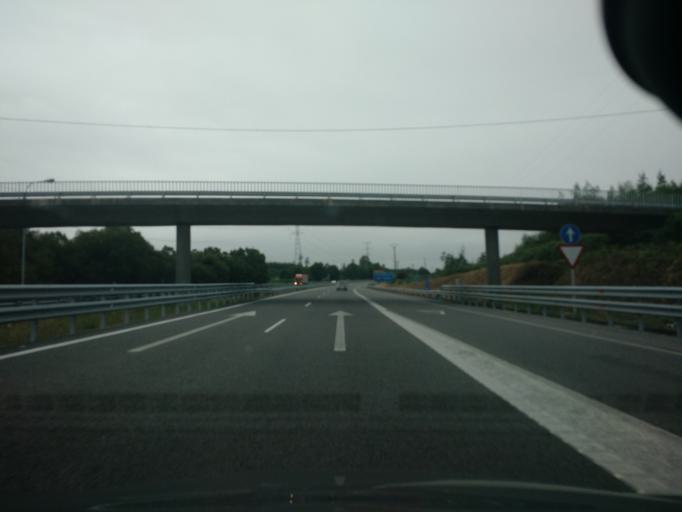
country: ES
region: Galicia
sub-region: Provincia da Coruna
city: Ordes
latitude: 43.0946
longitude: -8.3511
